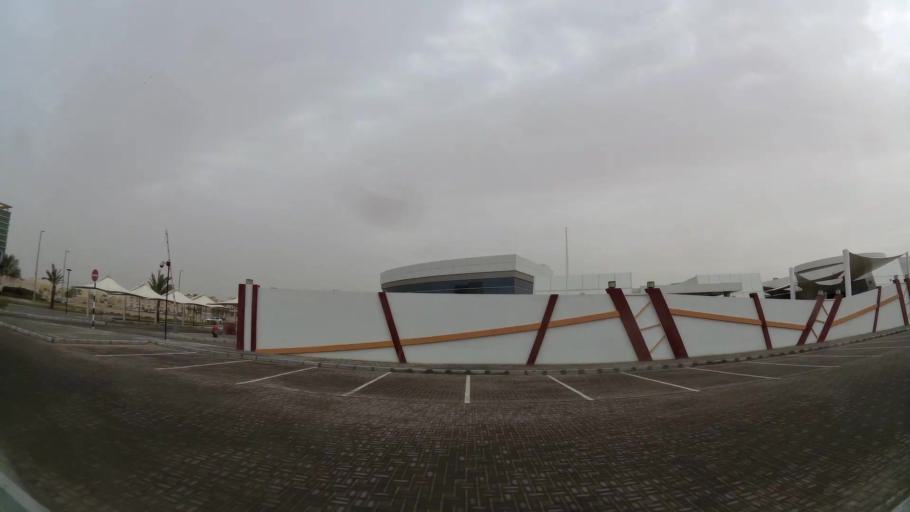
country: AE
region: Abu Dhabi
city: Abu Dhabi
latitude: 24.4326
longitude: 54.5829
